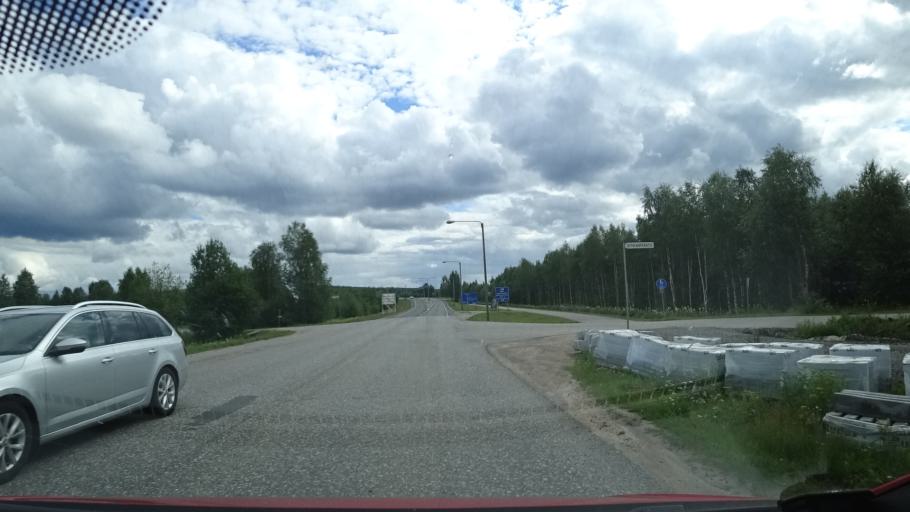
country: FI
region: Lapland
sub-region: Rovaniemi
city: Rovaniemi
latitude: 66.5225
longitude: 25.7459
